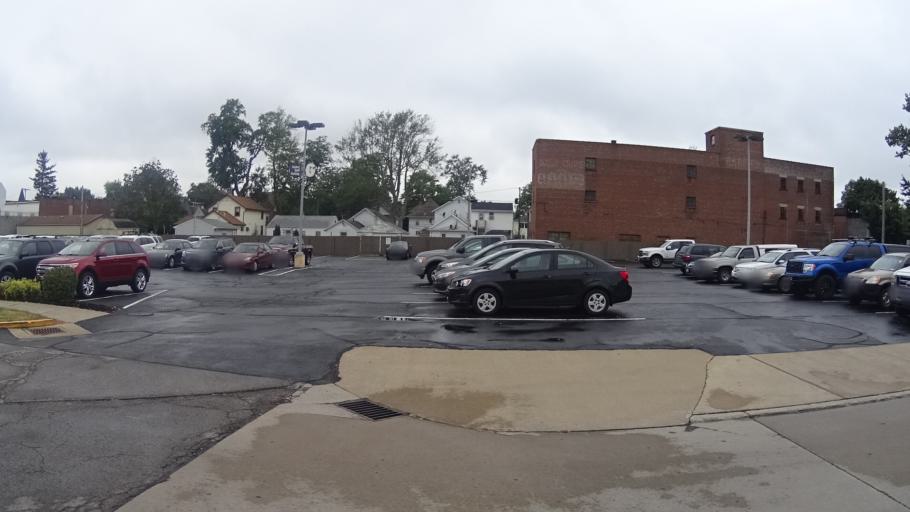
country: US
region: Ohio
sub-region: Erie County
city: Sandusky
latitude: 41.4459
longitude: -82.7125
